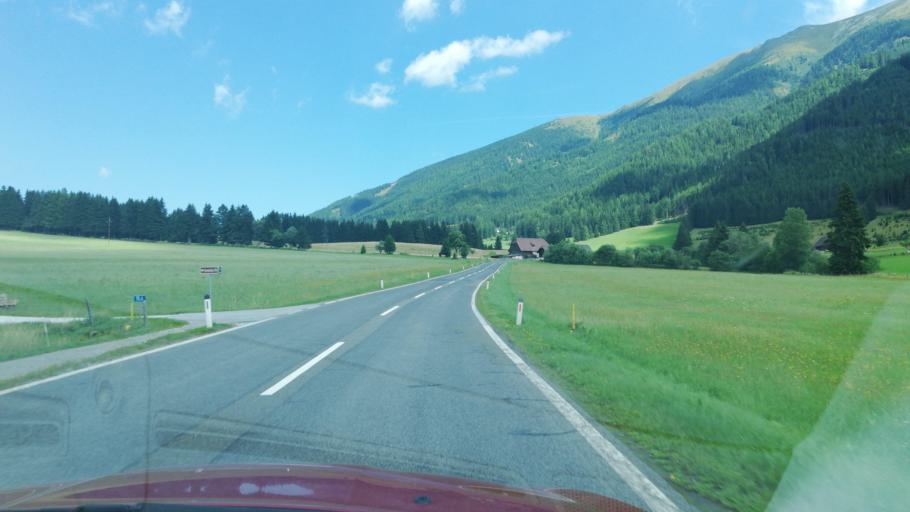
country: AT
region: Styria
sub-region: Politischer Bezirk Murtal
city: Sankt Johann am Tauern
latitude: 47.3854
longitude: 14.4634
